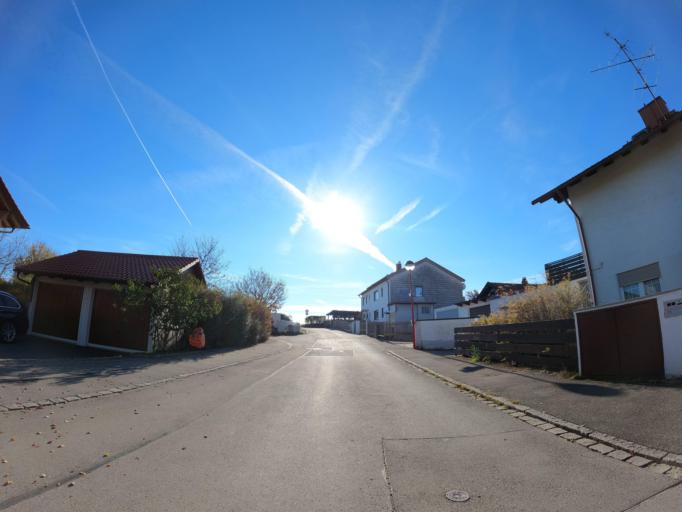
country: DE
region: Bavaria
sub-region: Upper Bavaria
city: Oberhaching
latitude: 48.0280
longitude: 11.6030
